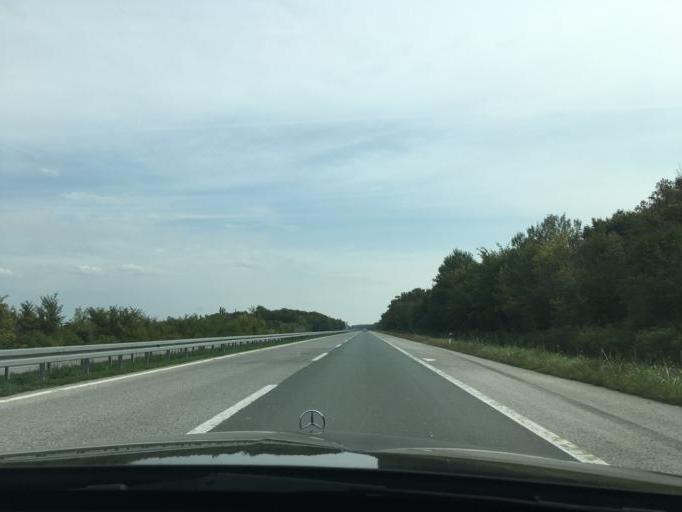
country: RS
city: Visnjicevo
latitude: 45.0435
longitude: 19.2488
